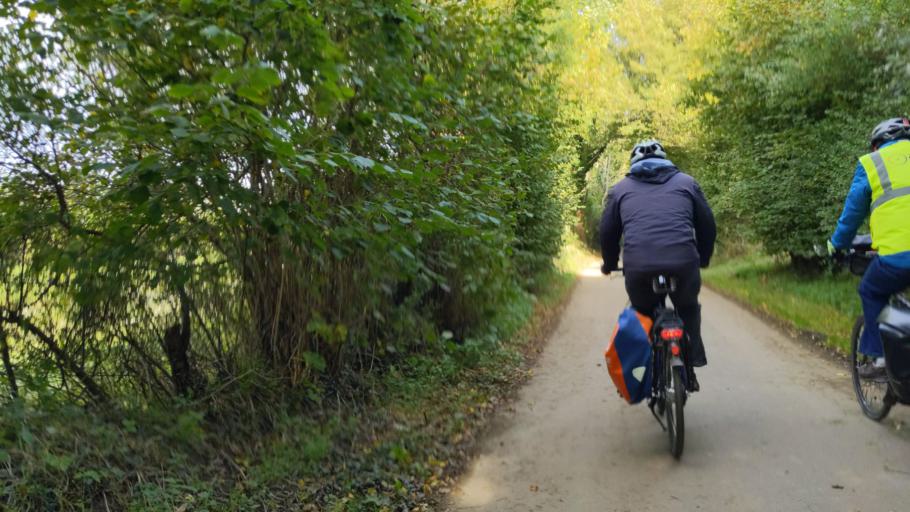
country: DE
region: Schleswig-Holstein
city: Zarpen
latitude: 53.8653
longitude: 10.5197
